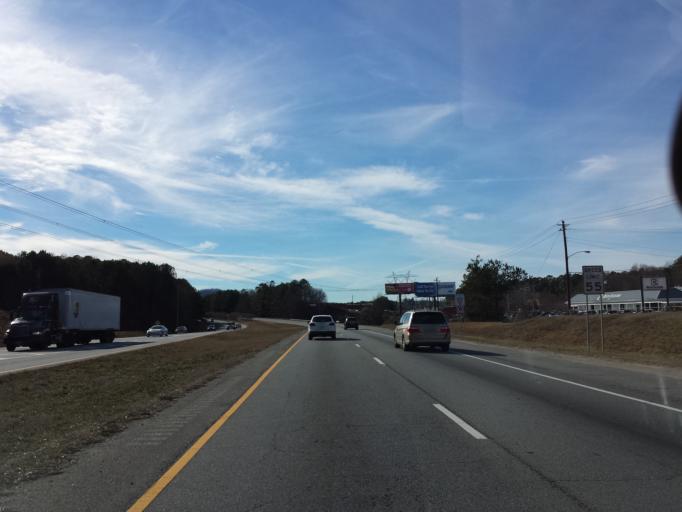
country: US
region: Georgia
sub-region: Cobb County
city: Marietta
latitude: 33.9975
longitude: -84.5293
